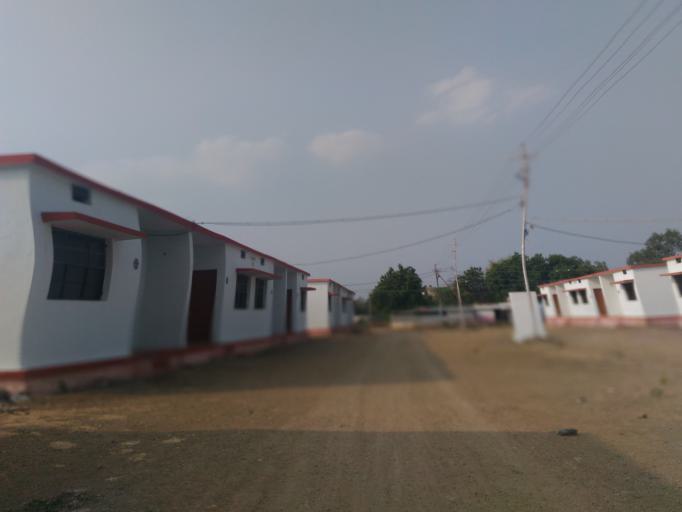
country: IN
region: Karnataka
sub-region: Raichur
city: Lingsugur
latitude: 16.1905
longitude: 76.6616
